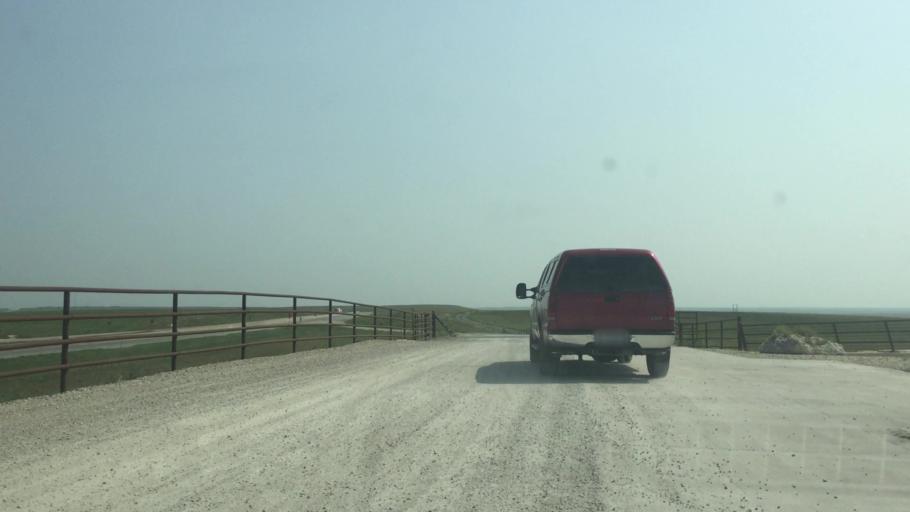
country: US
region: Kansas
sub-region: Chase County
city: Cottonwood Falls
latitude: 38.2292
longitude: -96.4085
